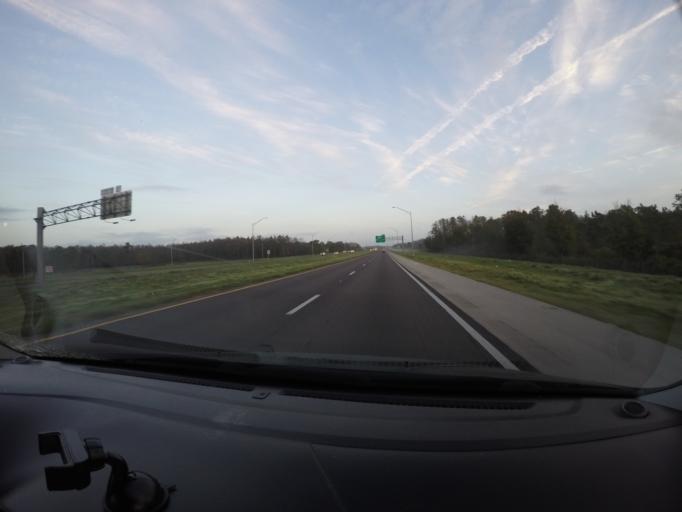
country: US
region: Florida
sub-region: Orange County
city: Conway
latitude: 28.4318
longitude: -81.2286
